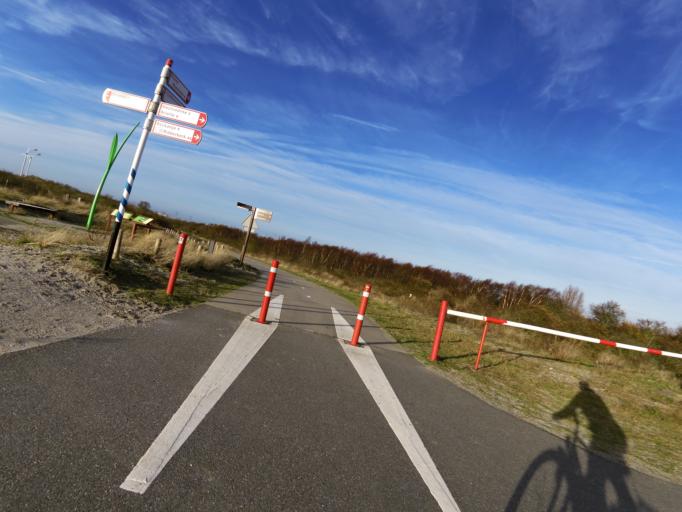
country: NL
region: South Holland
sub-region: Gemeente Rotterdam
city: Hoek van Holland
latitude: 51.9155
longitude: 4.0629
